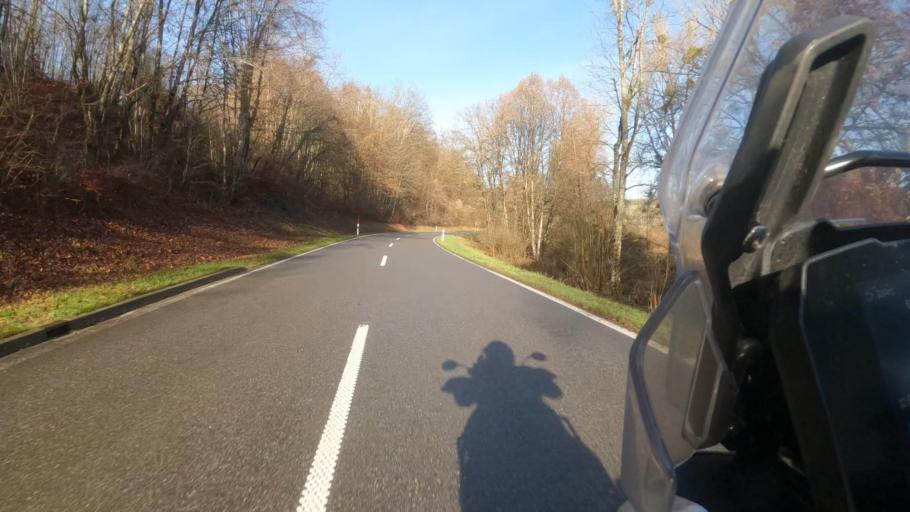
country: DE
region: Baden-Wuerttemberg
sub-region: Freiburg Region
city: Neuhausen
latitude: 47.8110
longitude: 8.7350
